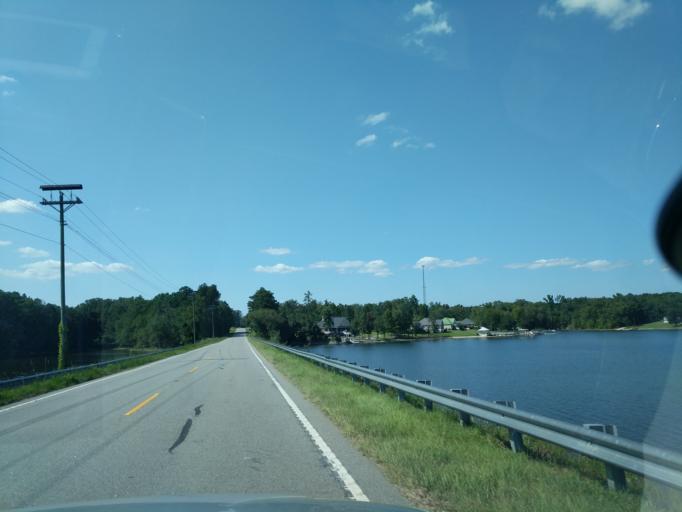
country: US
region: South Carolina
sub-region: Newberry County
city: Prosperity
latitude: 34.0834
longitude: -81.5646
